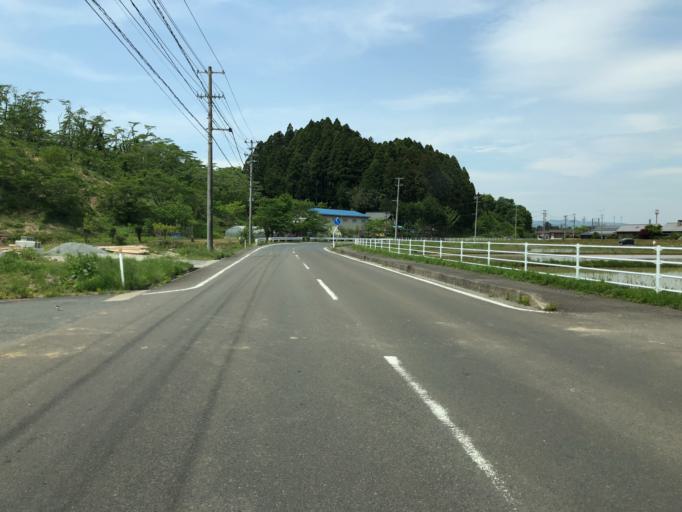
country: JP
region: Fukushima
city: Namie
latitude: 37.6962
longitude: 140.9656
